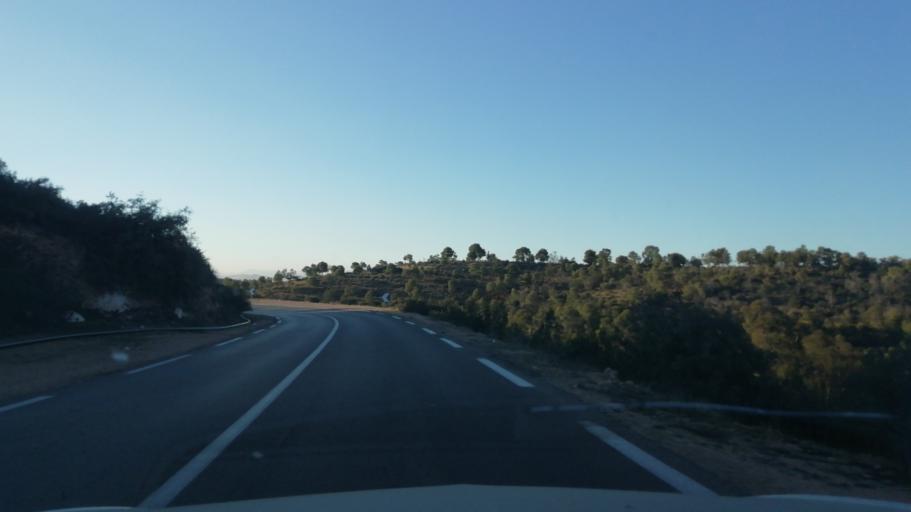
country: DZ
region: Tlemcen
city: Beni Mester
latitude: 34.8130
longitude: -1.6223
